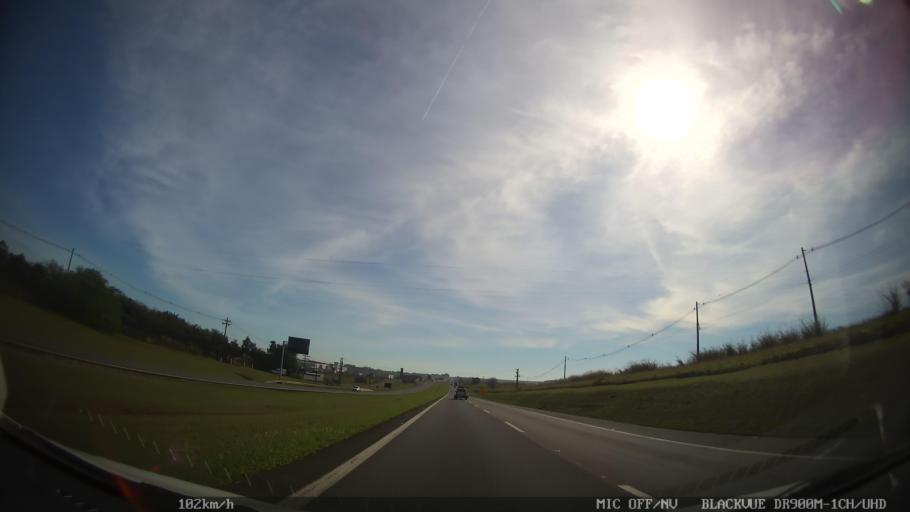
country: BR
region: Sao Paulo
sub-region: Cordeiropolis
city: Cordeiropolis
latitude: -22.4981
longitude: -47.3995
